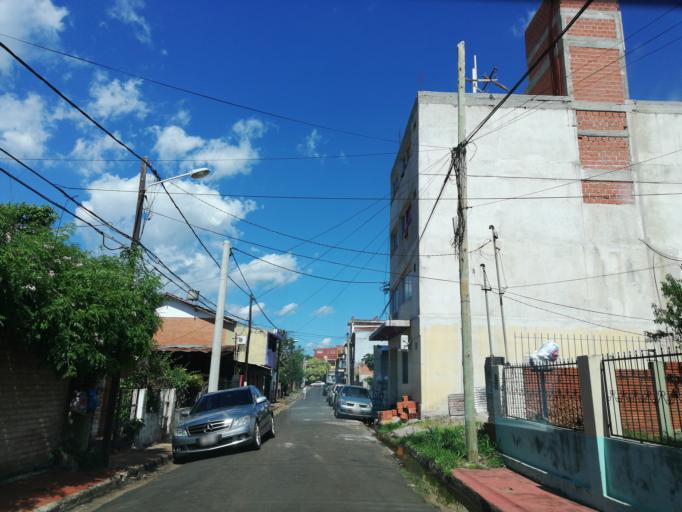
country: AR
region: Misiones
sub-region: Departamento de Capital
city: Posadas
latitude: -27.3654
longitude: -55.9064
